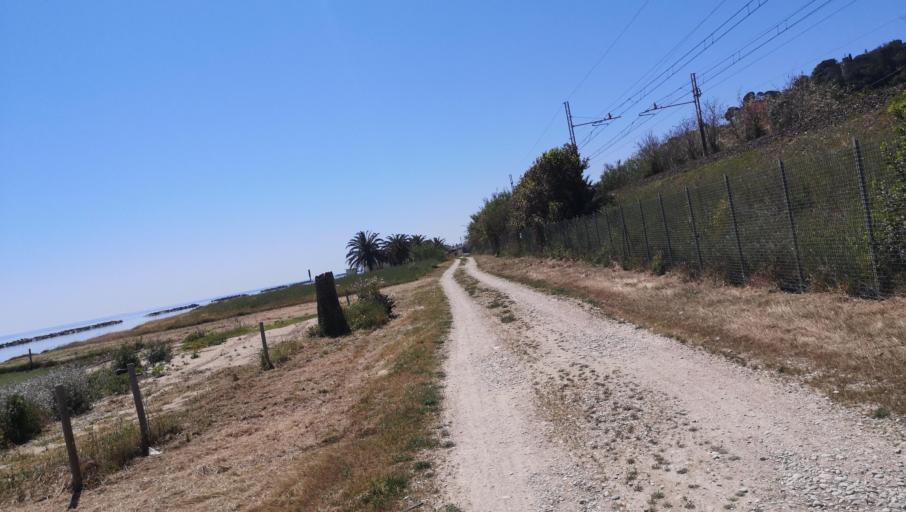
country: IT
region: The Marches
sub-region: Provincia di Ascoli Piceno
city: Cupra Marittima
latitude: 43.0562
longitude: 13.8513
